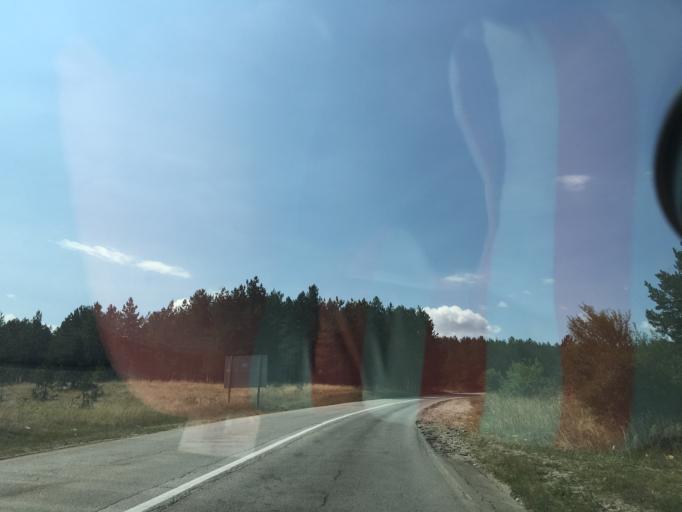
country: RS
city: Zlatibor
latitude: 43.7209
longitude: 19.7061
